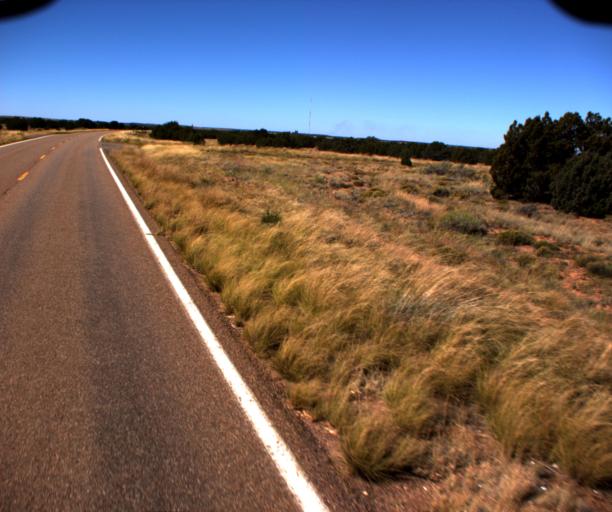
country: US
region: Arizona
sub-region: Navajo County
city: Heber-Overgaard
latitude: 34.4639
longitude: -110.3792
